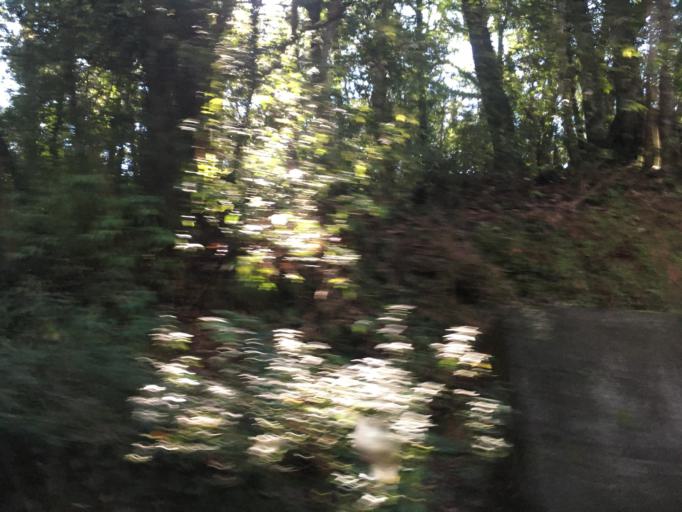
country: TW
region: Taiwan
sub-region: Yilan
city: Yilan
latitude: 24.7570
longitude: 121.5922
